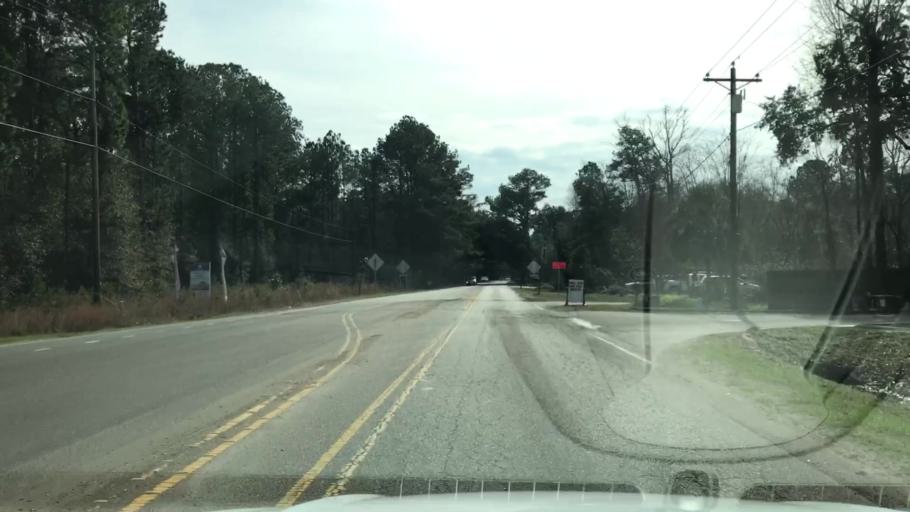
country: US
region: South Carolina
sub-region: Charleston County
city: Shell Point
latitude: 32.7429
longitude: -80.0379
